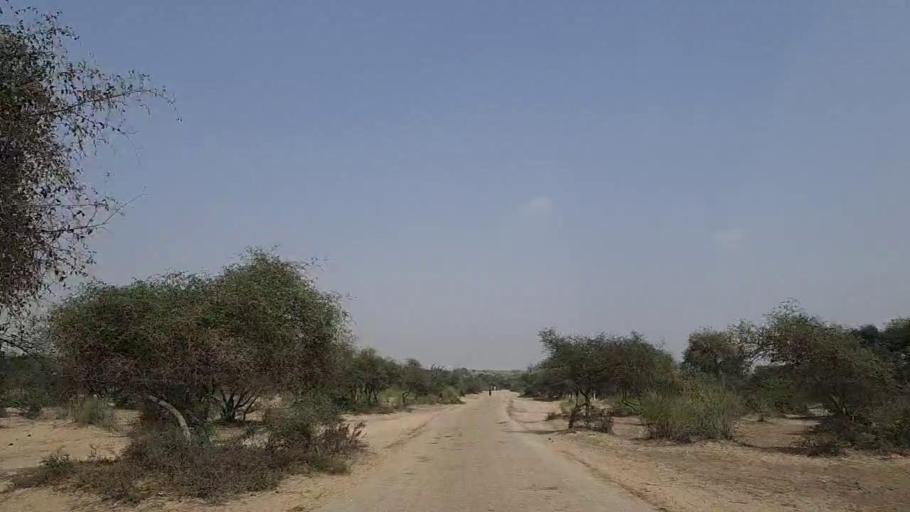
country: PK
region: Sindh
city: Mithi
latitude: 24.7576
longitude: 69.9266
